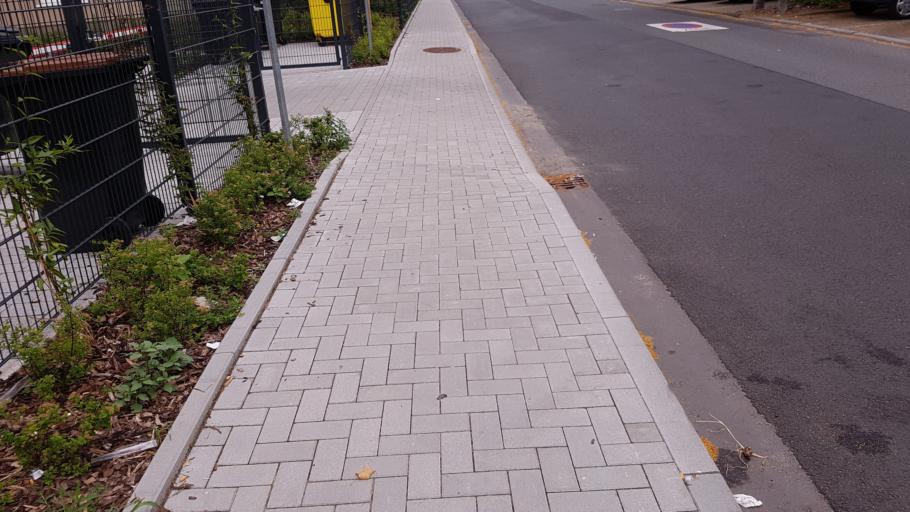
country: DE
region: Hesse
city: Kelsterbach
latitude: 50.0553
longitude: 8.5277
